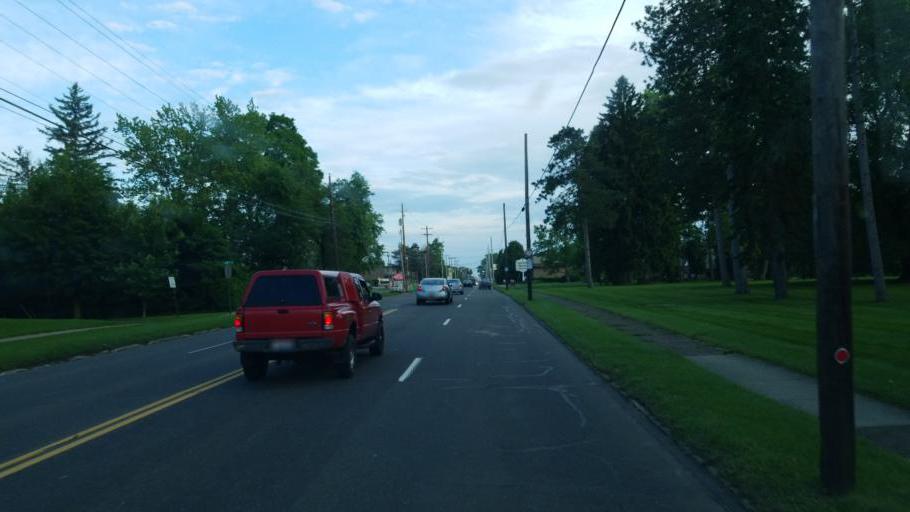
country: US
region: Ohio
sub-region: Stark County
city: North Canton
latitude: 40.8528
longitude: -81.3938
